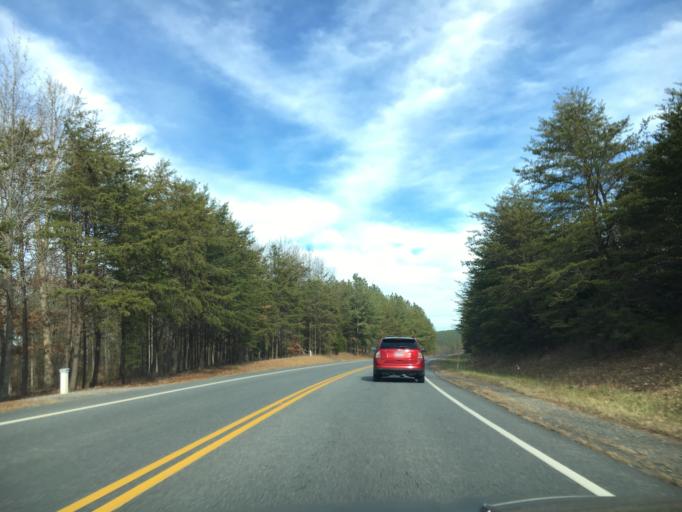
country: US
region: Virginia
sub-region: Louisa County
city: Louisa
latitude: 38.0589
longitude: -77.8811
